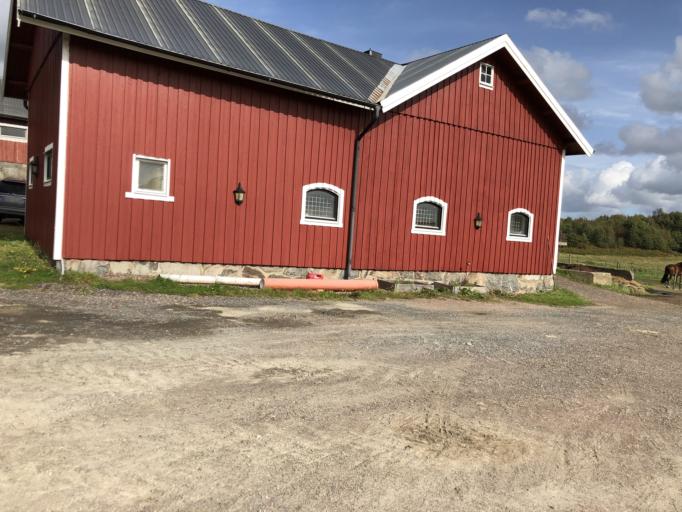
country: SE
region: Vaestra Goetaland
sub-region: Goteborg
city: Majorna
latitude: 57.7614
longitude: 11.8631
